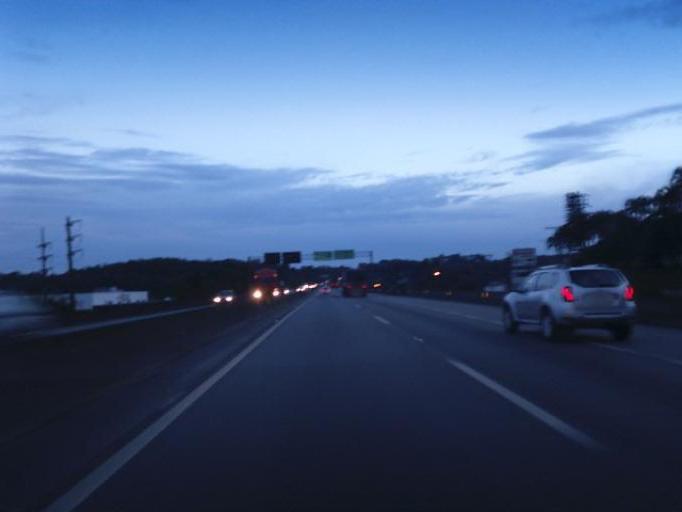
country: BR
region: Santa Catarina
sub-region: Joinville
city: Joinville
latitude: -26.3243
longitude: -48.8671
